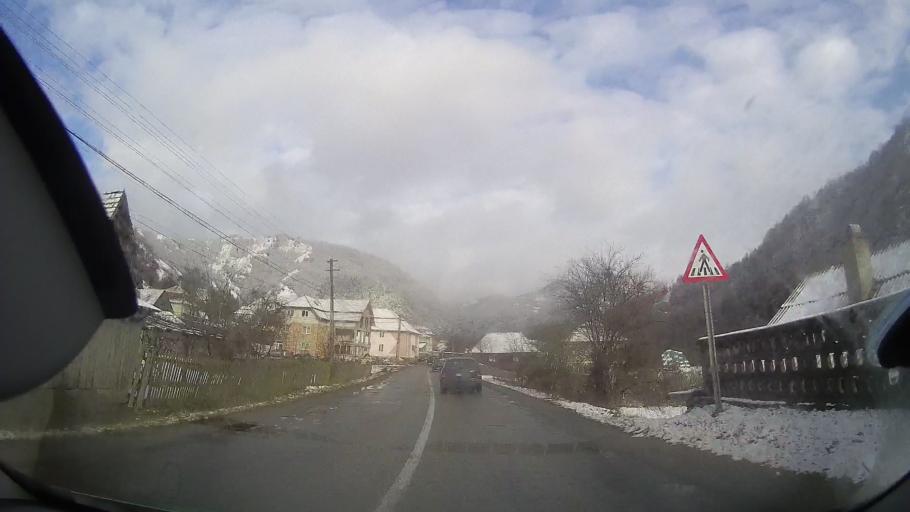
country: RO
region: Alba
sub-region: Oras Baia de Aries
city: Baia de Aries
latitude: 46.3919
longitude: 23.2997
